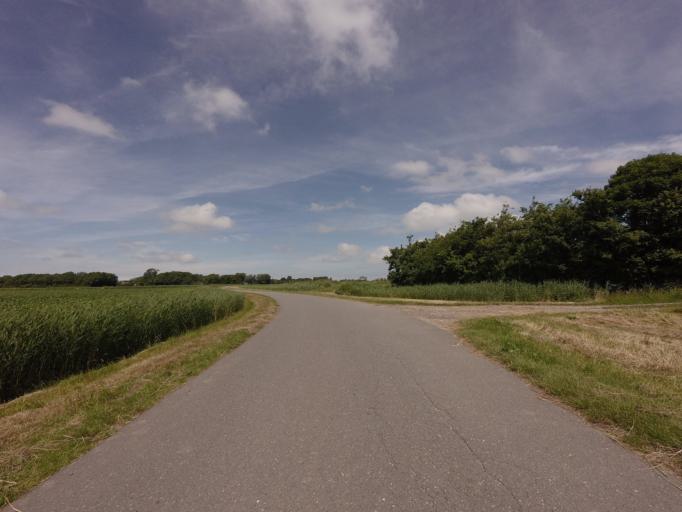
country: NL
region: North Holland
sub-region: Gemeente Texel
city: Den Burg
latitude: 53.0798
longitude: 4.8819
